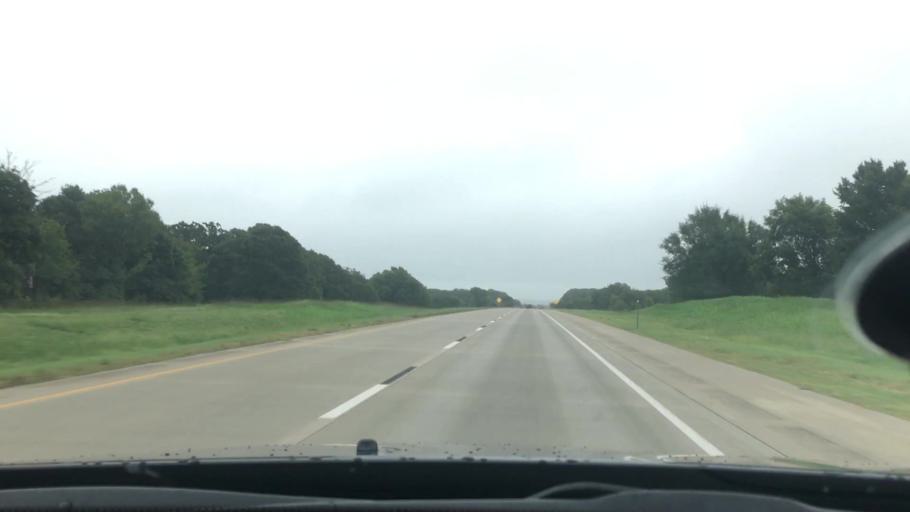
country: US
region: Oklahoma
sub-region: Okfuskee County
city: Boley
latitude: 35.3841
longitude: -96.5715
